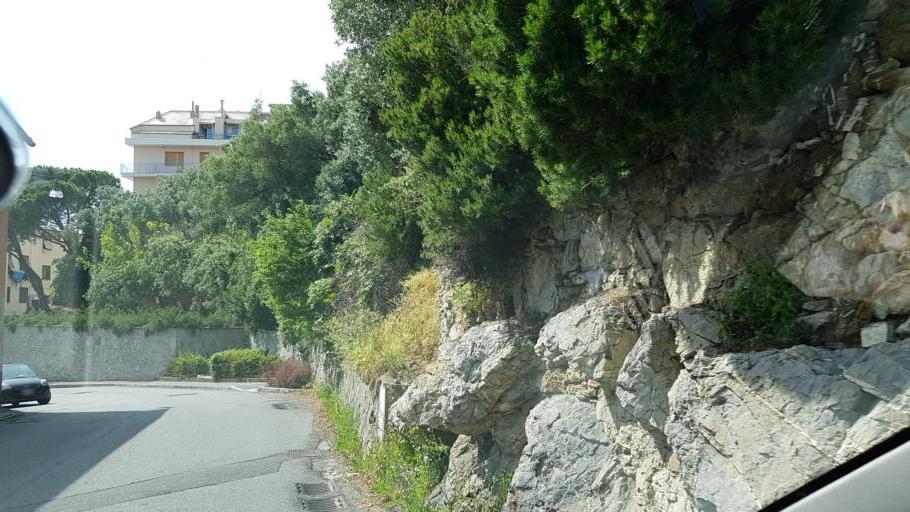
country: IT
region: Liguria
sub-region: Provincia di Genova
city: Genoa
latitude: 44.4011
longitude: 8.9909
